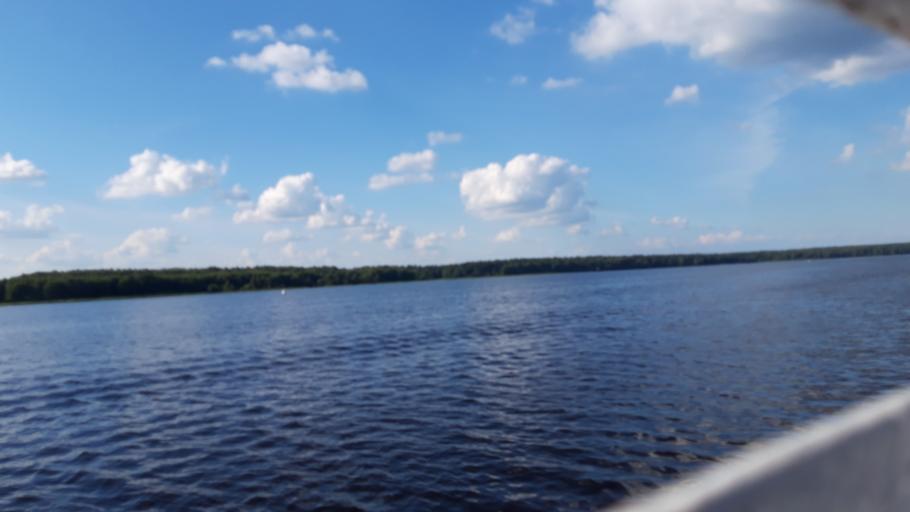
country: RU
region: Tverskaya
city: Konakovo
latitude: 56.6828
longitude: 36.6868
